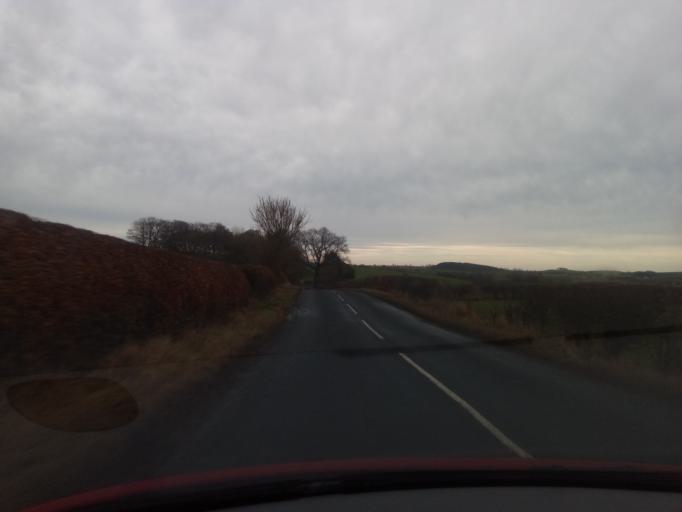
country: GB
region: England
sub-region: Northumberland
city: Ellingham
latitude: 55.4599
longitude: -1.8064
